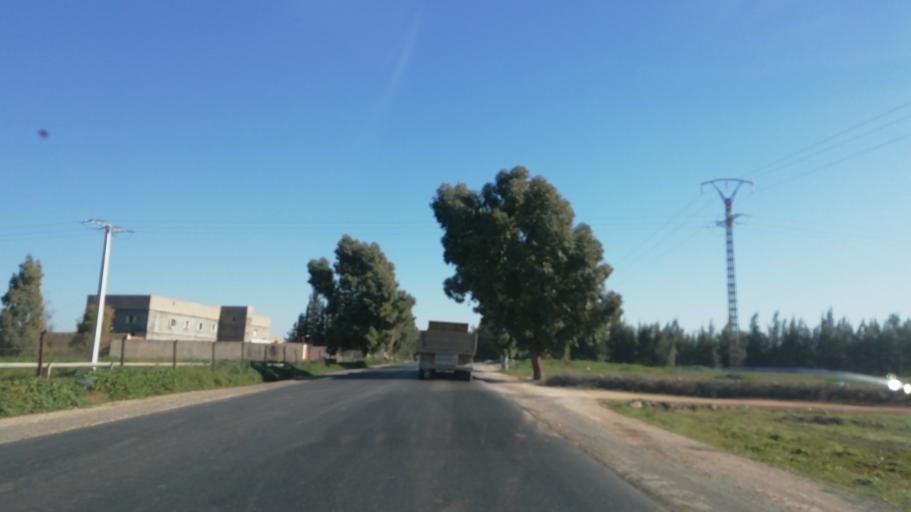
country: DZ
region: Relizane
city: Zemoura
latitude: 35.7583
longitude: 0.6662
